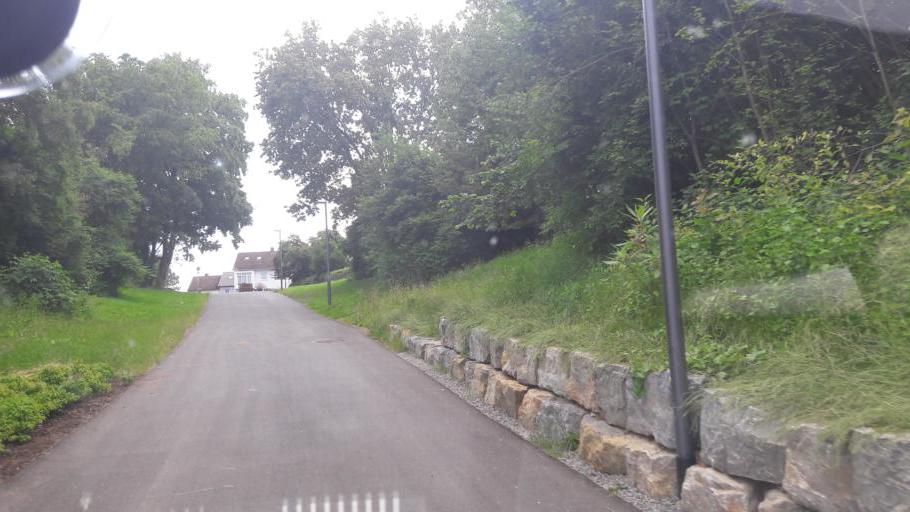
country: DE
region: Baden-Wuerttemberg
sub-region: Regierungsbezirk Stuttgart
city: Ohringen
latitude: 49.1961
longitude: 9.5118
